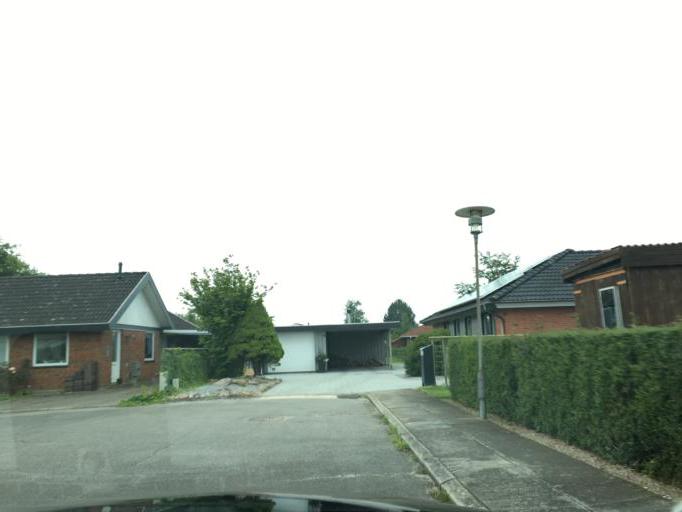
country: DK
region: South Denmark
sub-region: Kolding Kommune
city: Kolding
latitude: 55.5654
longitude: 9.4825
